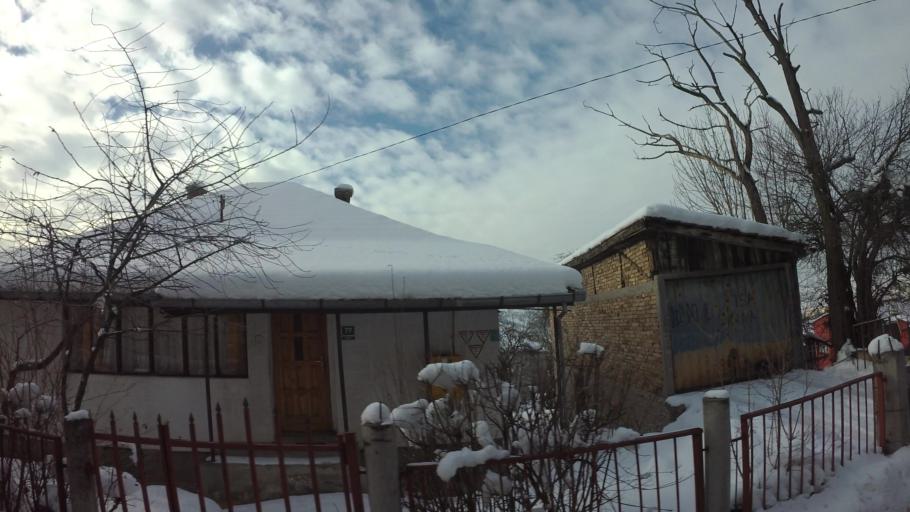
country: BA
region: Federation of Bosnia and Herzegovina
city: Kobilja Glava
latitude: 43.8769
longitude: 18.4174
